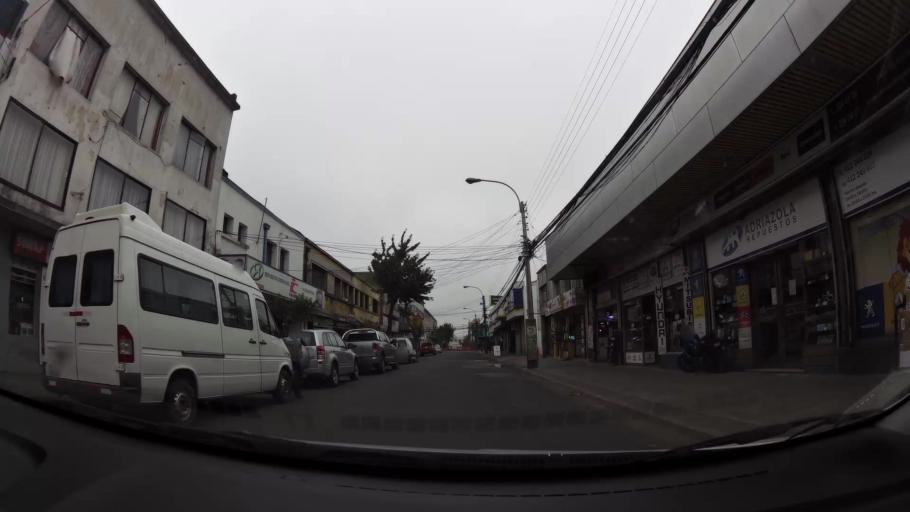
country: CL
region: Biobio
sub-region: Provincia de Concepcion
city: Concepcion
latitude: -36.8267
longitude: -73.0573
